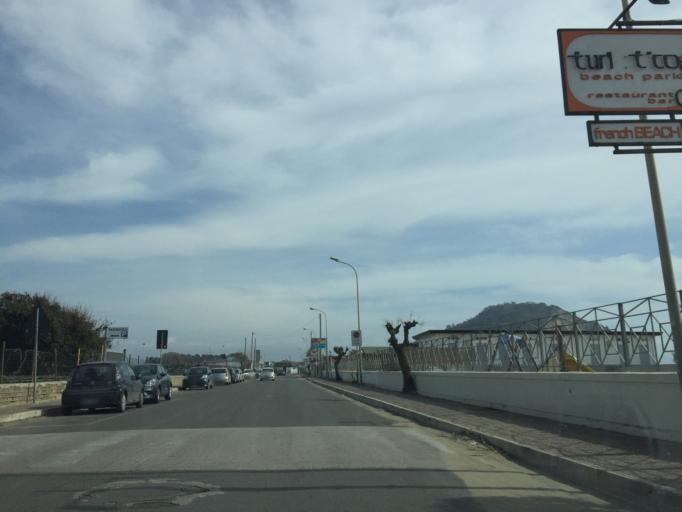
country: IT
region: Campania
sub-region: Provincia di Napoli
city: Bacoli
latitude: 40.7887
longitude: 14.0722
